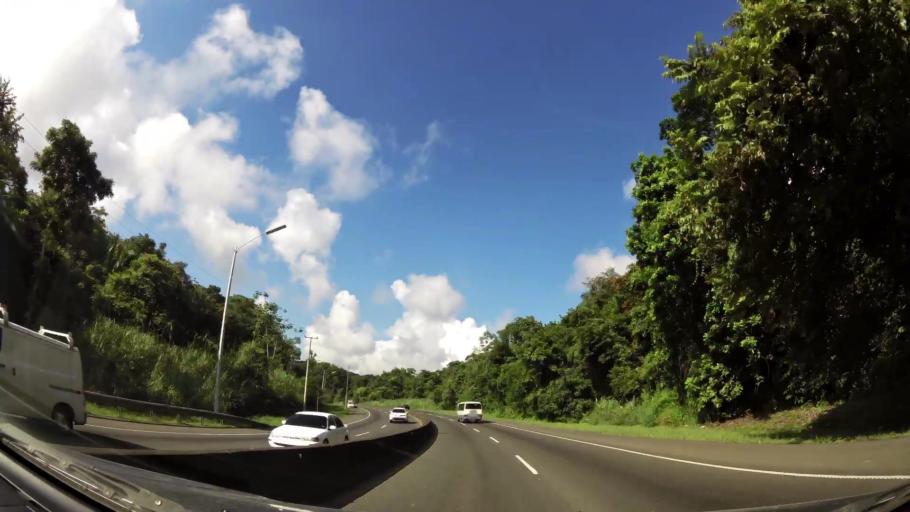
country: PA
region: Panama
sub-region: Distrito Arraijan
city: Arraijan
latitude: 8.9567
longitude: -79.6203
